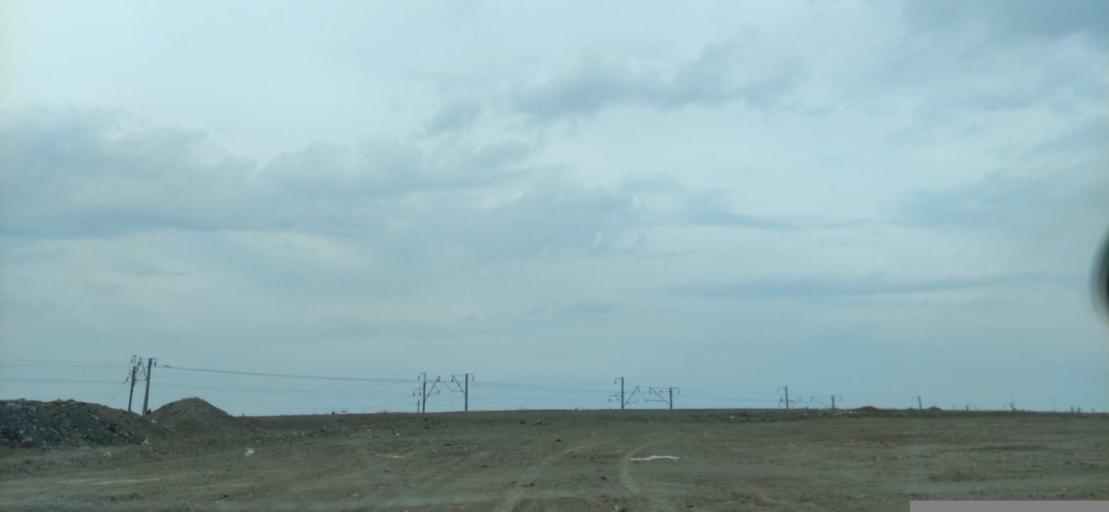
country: KZ
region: Qaraghandy
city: Saryshaghan
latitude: 46.0943
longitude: 73.6045
